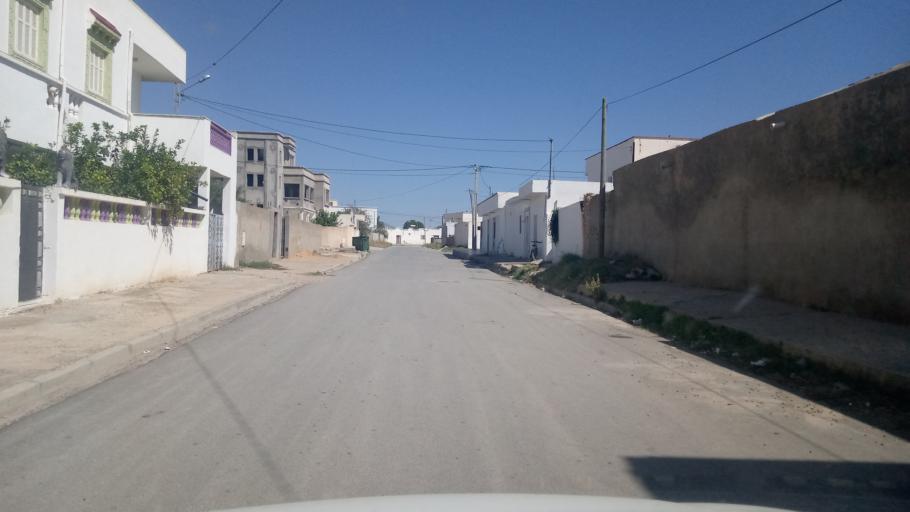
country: TN
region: Al Qayrawan
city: Sbikha
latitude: 36.1173
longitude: 10.0899
